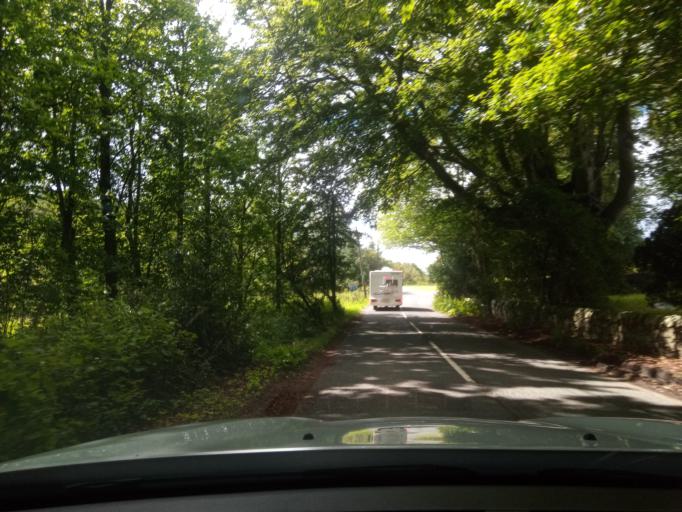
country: GB
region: Scotland
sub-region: The Scottish Borders
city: Innerleithen
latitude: 55.5392
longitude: -3.0181
